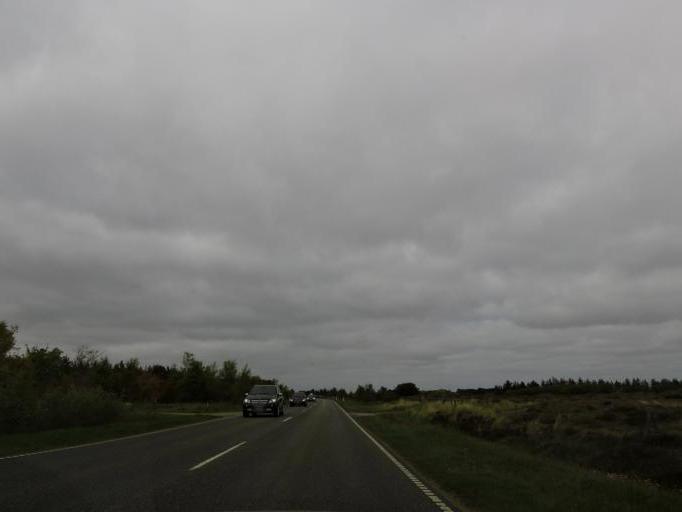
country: DE
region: Schleswig-Holstein
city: List
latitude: 55.1159
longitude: 8.5452
